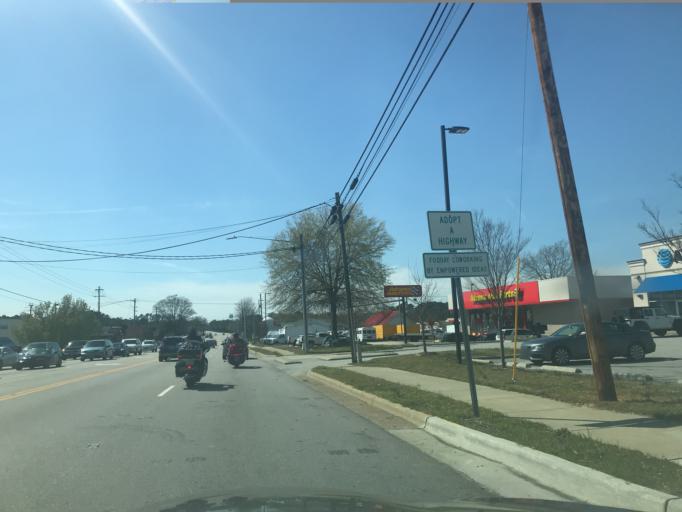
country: US
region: North Carolina
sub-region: Wake County
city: Fuquay-Varina
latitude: 35.5919
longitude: -78.7793
